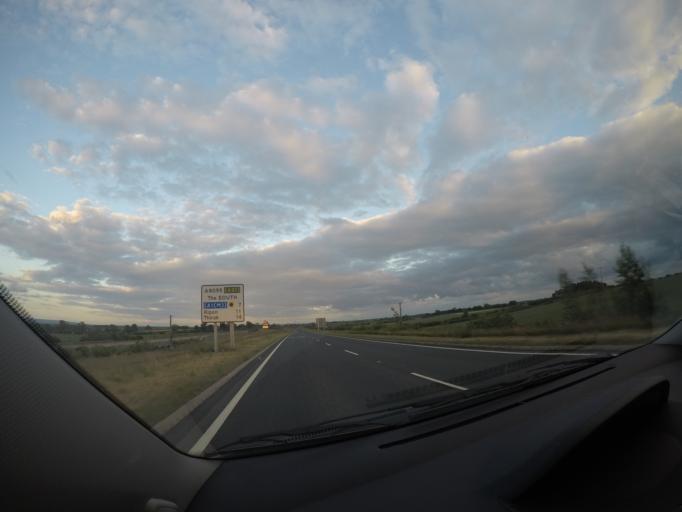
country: GB
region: England
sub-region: North Yorkshire
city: Bedale
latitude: 54.2718
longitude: -1.5273
